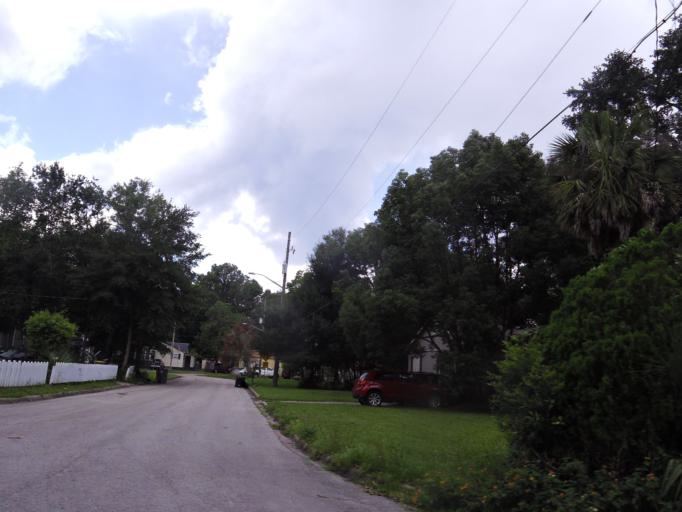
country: US
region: Florida
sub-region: Duval County
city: Jacksonville
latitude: 30.3025
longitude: -81.6321
